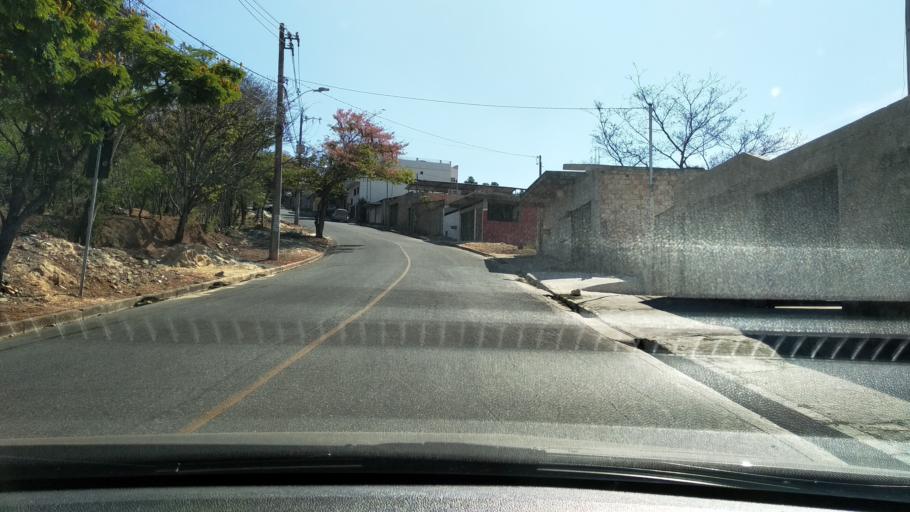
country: BR
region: Minas Gerais
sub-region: Belo Horizonte
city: Belo Horizonte
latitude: -19.8621
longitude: -43.8789
